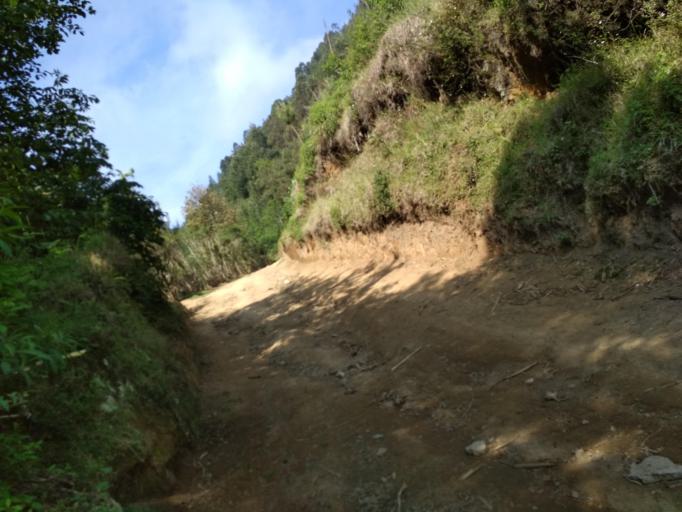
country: MX
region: Veracruz
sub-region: Mariano Escobedo
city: San Isidro el Berro
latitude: 18.9418
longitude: -97.2191
